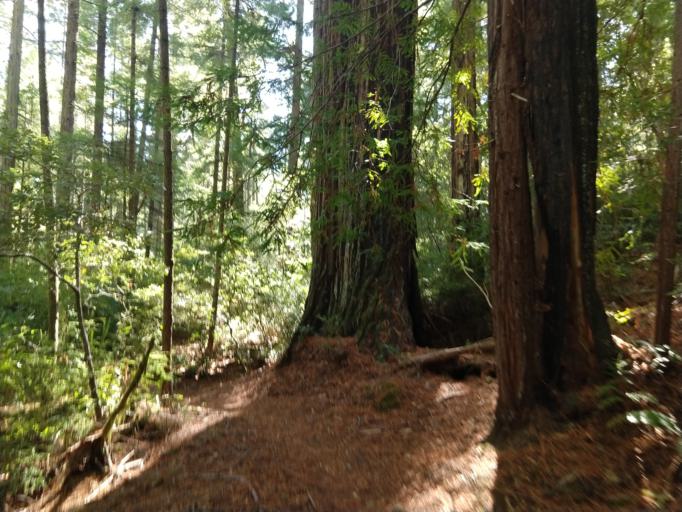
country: US
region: California
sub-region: Humboldt County
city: Rio Dell
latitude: 40.3585
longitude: -123.9950
